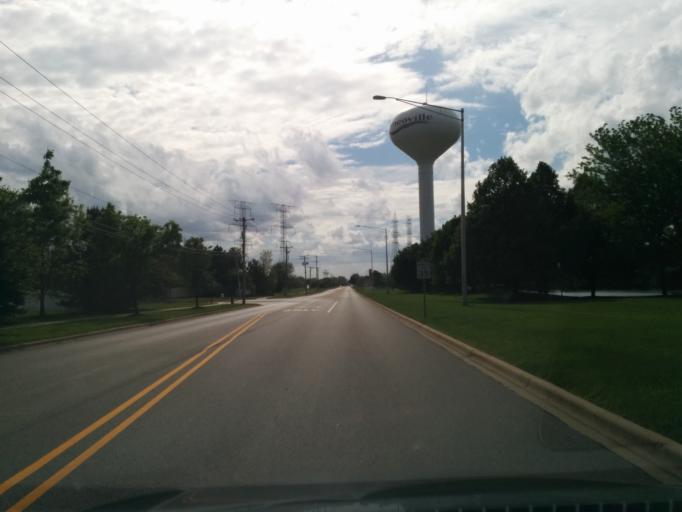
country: US
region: Illinois
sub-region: Will County
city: Romeoville
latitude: 41.6240
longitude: -88.1359
